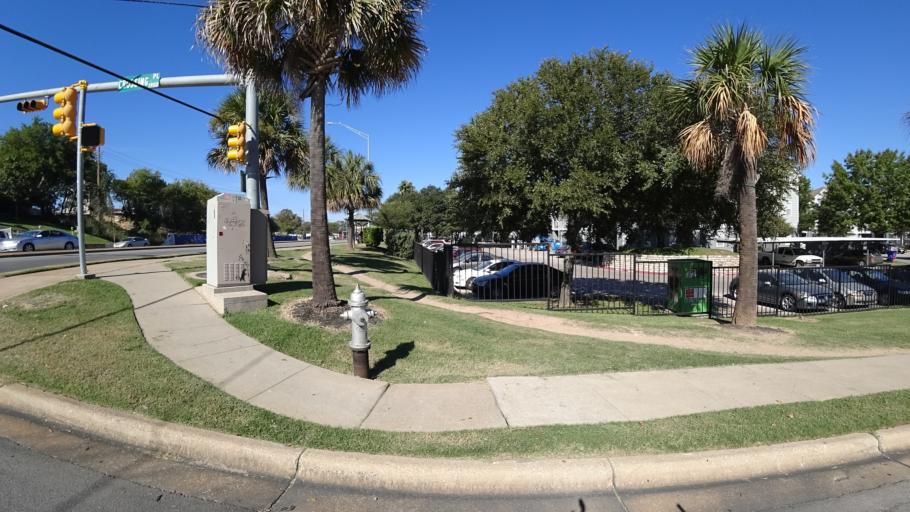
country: US
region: Texas
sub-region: Travis County
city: Austin
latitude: 30.2319
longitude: -97.7174
